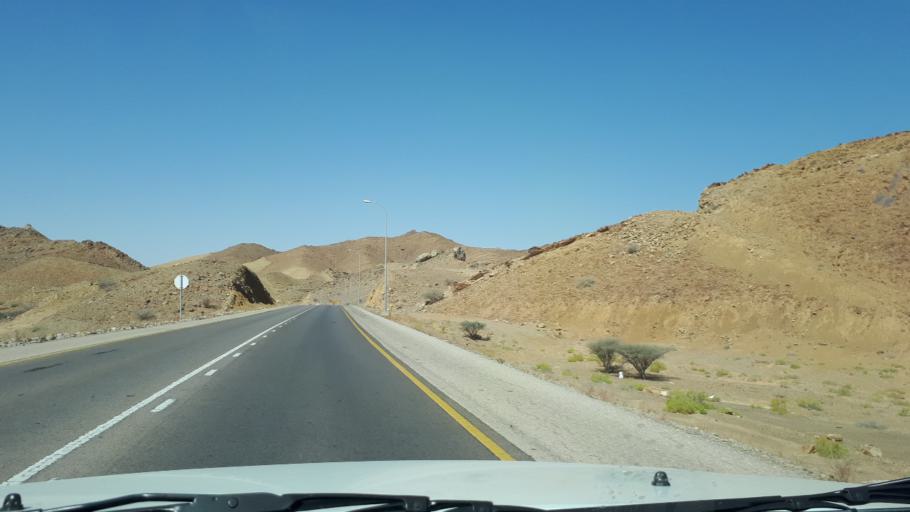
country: OM
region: Ash Sharqiyah
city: Sur
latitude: 22.3387
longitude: 59.3125
